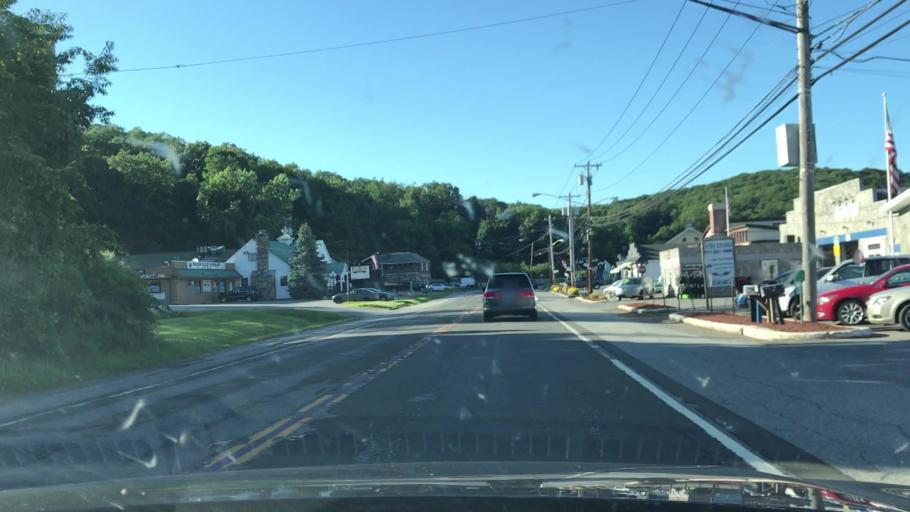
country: US
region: New York
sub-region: Putnam County
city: Mahopac
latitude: 41.3587
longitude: -73.7470
